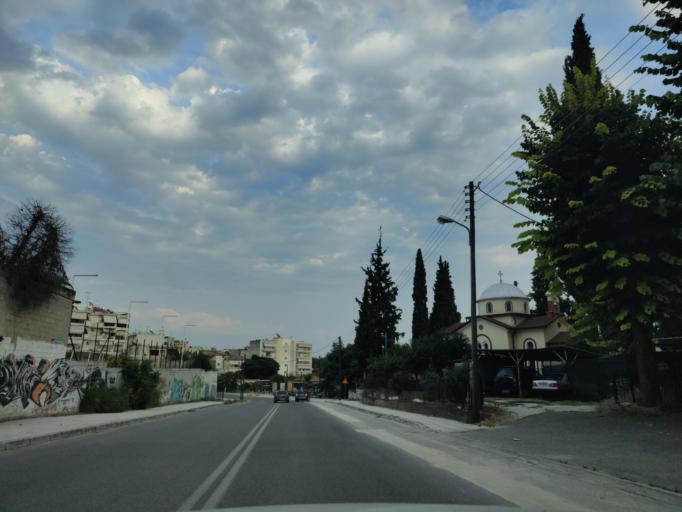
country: GR
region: East Macedonia and Thrace
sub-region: Nomos Dramas
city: Drama
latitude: 41.1505
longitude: 24.1350
